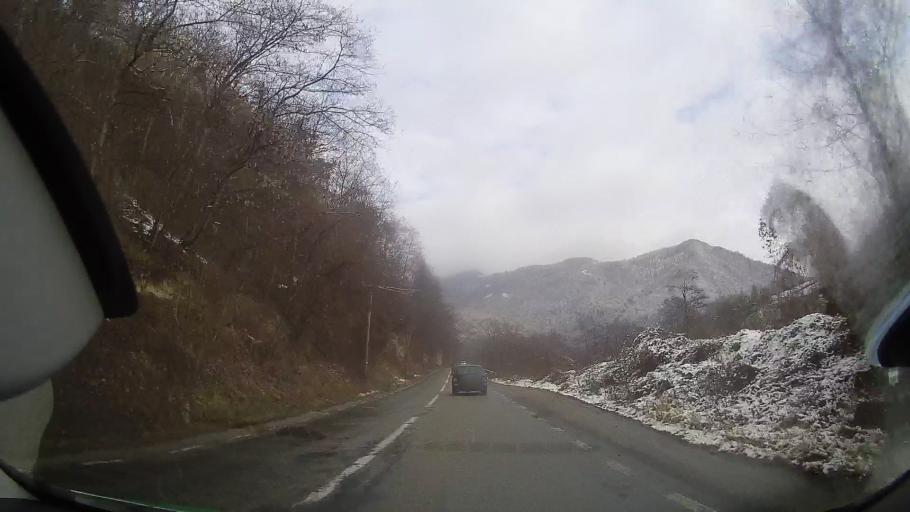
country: RO
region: Alba
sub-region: Oras Baia de Aries
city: Baia de Aries
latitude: 46.4022
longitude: 23.3225
